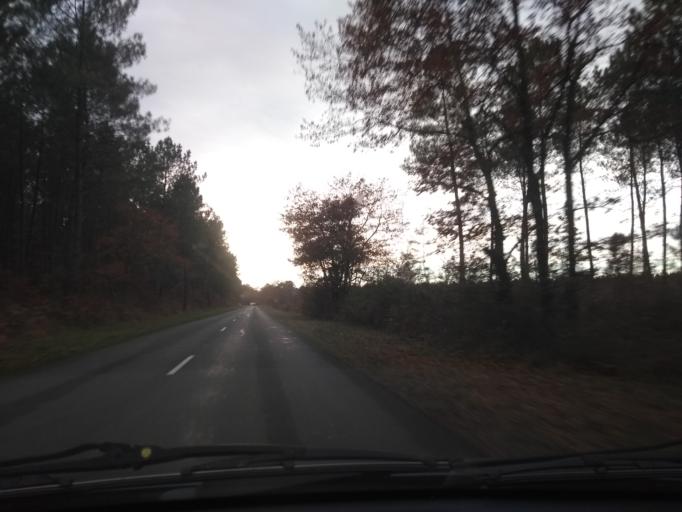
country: FR
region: Aquitaine
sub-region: Departement de la Gironde
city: Saucats
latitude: 44.6451
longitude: -0.6255
